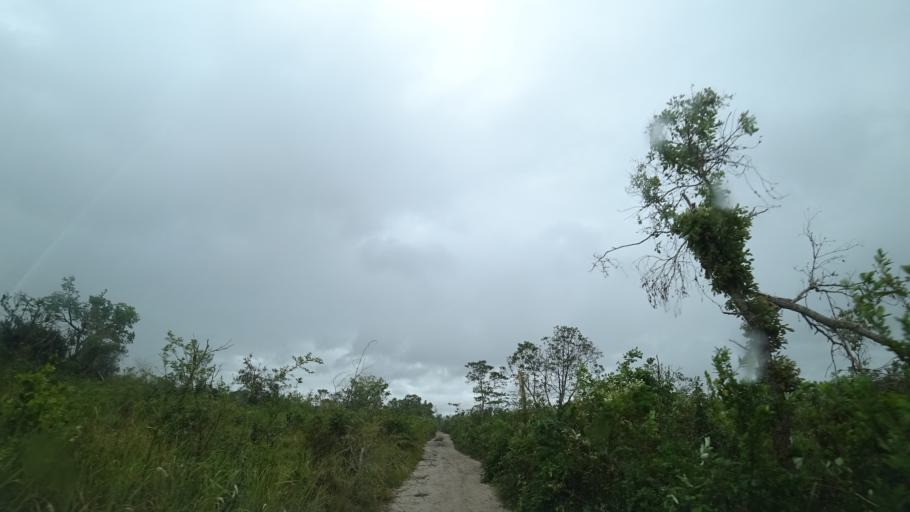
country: MZ
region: Sofala
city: Dondo
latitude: -19.5534
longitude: 35.0592
